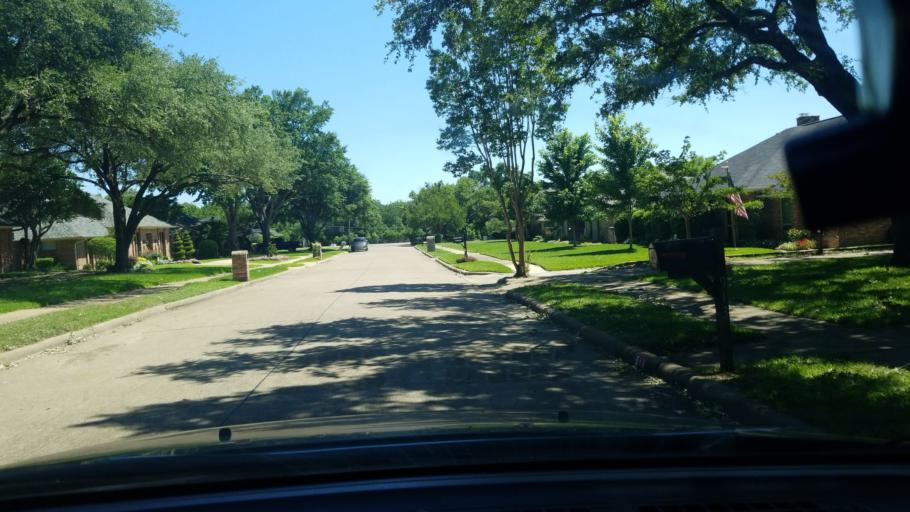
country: US
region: Texas
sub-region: Dallas County
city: Mesquite
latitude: 32.7571
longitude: -96.6011
